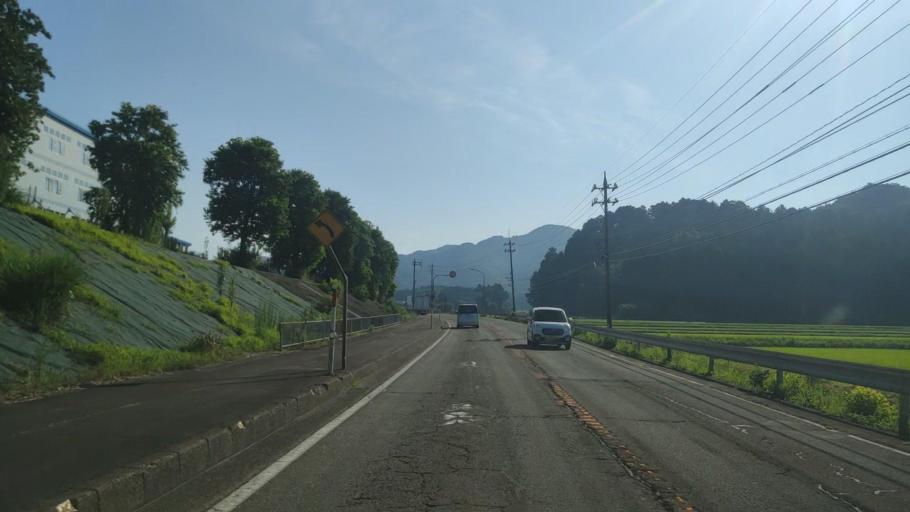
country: JP
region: Fukui
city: Maruoka
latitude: 36.2271
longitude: 136.2836
